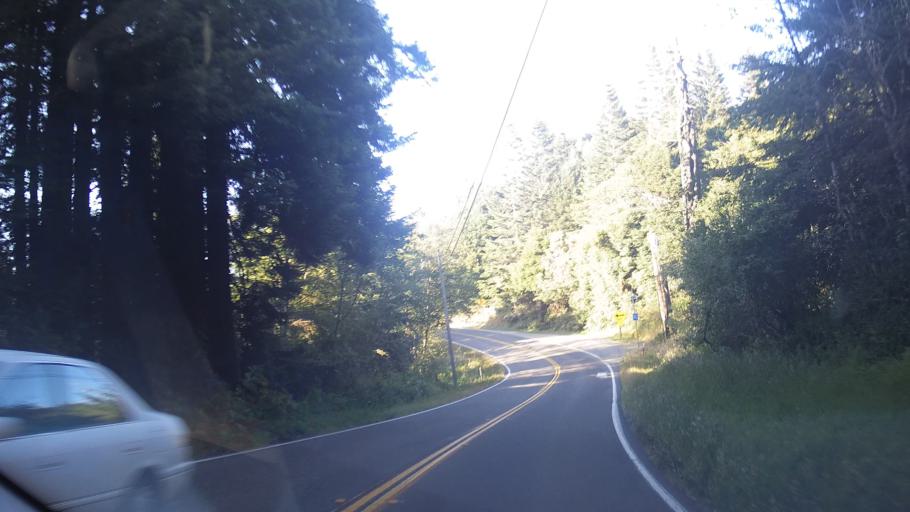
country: US
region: California
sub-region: Mendocino County
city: Fort Bragg
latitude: 39.5087
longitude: -123.7654
